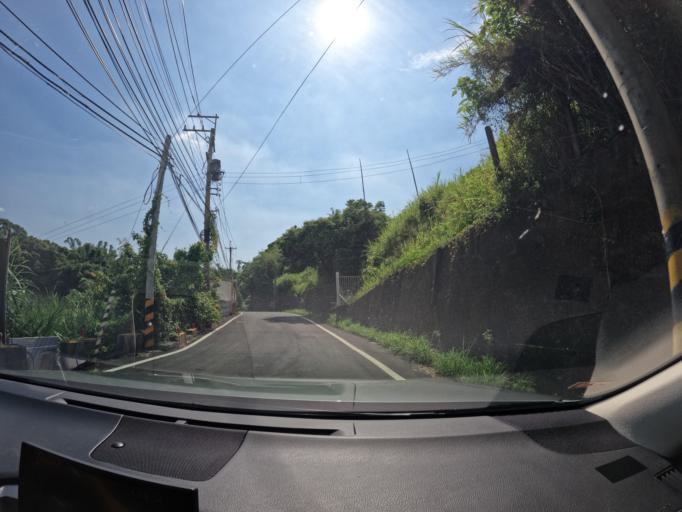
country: TW
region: Taiwan
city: Fengyuan
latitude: 24.3120
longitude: 120.7487
